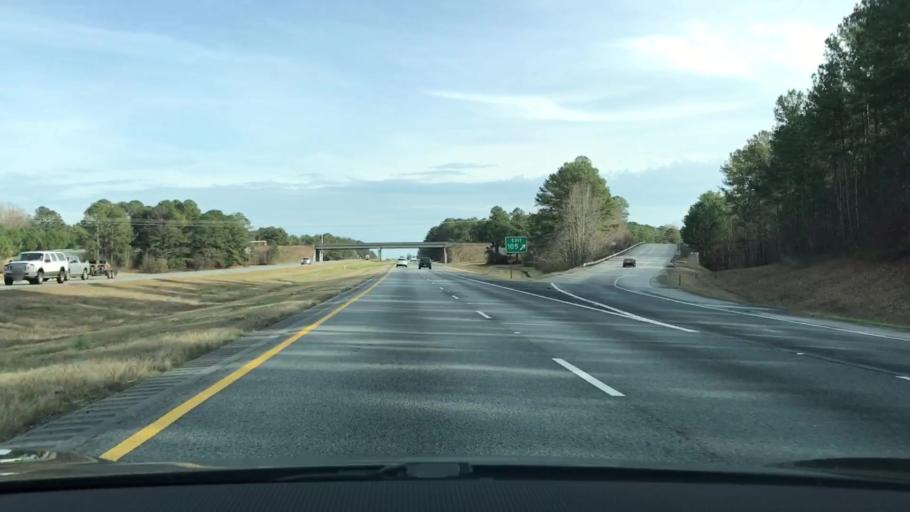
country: US
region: Georgia
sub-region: Walton County
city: Social Circle
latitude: 33.5944
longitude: -83.6347
